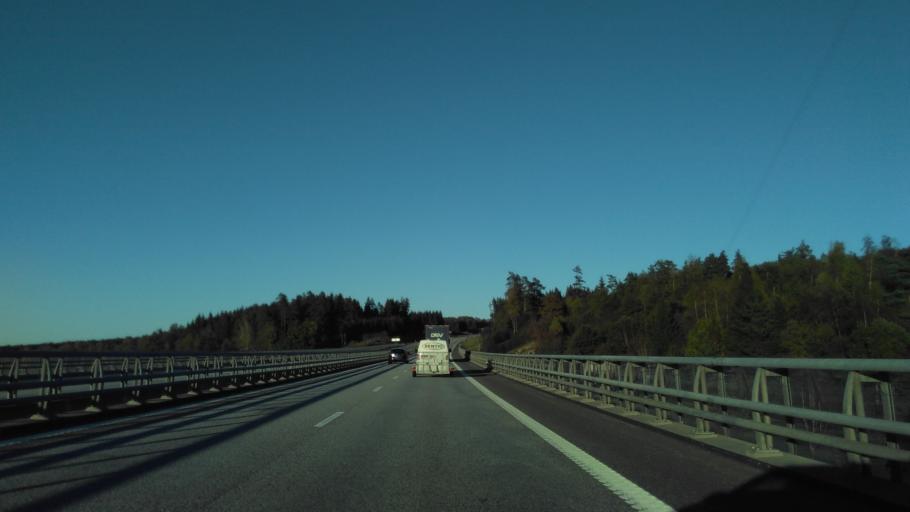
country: SE
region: Vaestra Goetaland
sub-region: Boras Kommun
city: Dalsjofors
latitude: 57.7864
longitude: 13.1263
